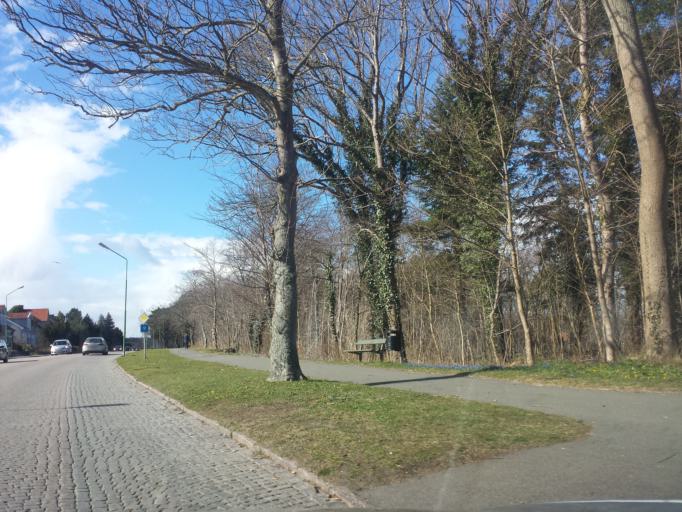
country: SE
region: Skane
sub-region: Simrishamns Kommun
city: Simrishamn
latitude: 55.5602
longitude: 14.3422
